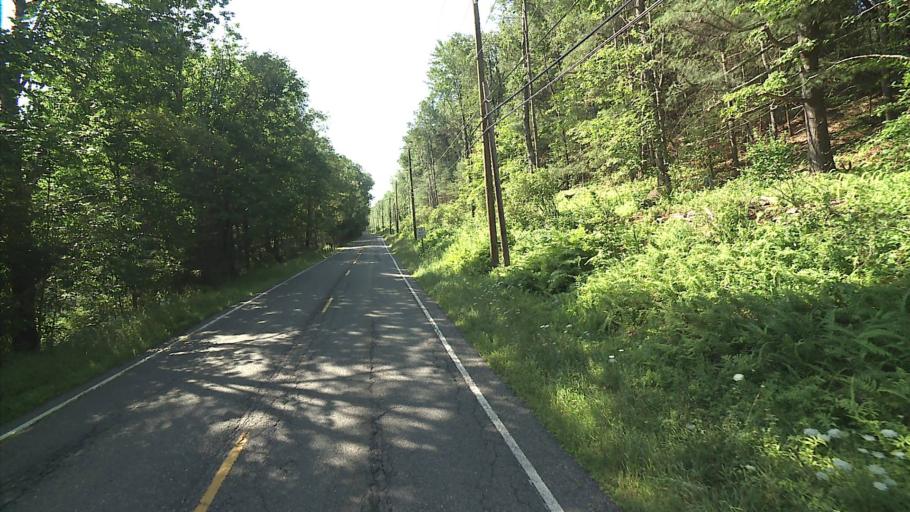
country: US
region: Connecticut
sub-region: Litchfield County
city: Winsted
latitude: 42.0016
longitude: -73.1037
